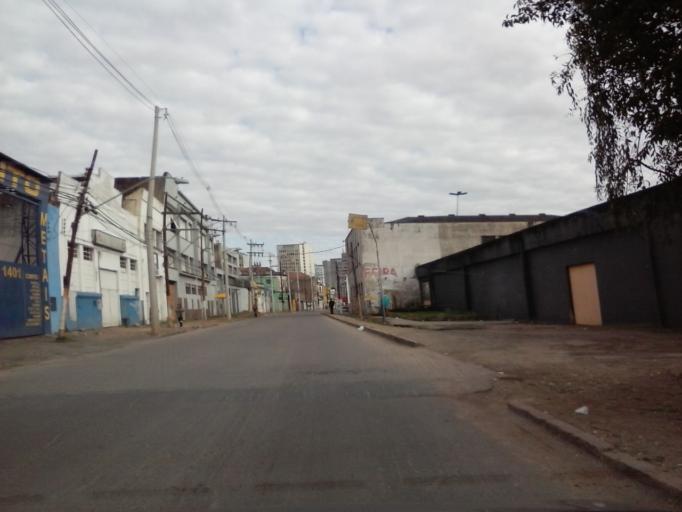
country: BR
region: Rio Grande do Sul
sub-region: Porto Alegre
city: Porto Alegre
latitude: -30.0215
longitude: -51.2151
